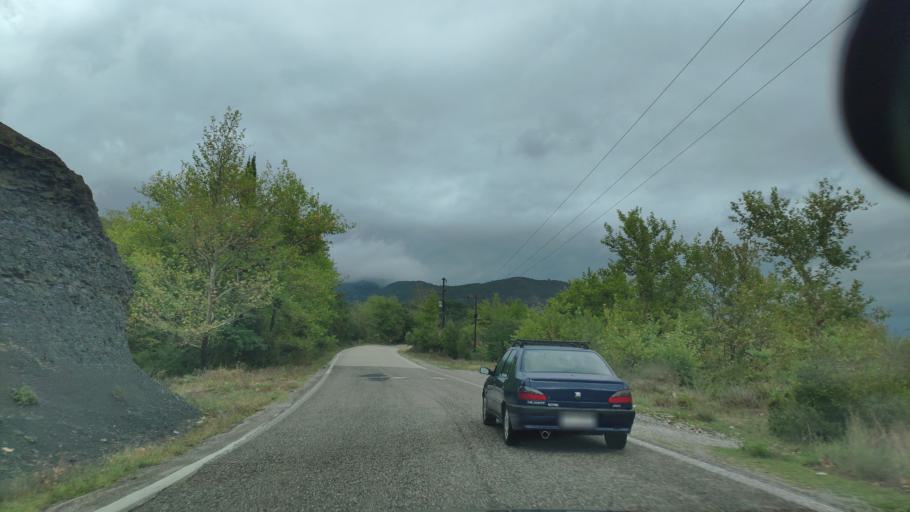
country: GR
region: West Greece
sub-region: Nomos Aitolias kai Akarnanias
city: Krikellos
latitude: 38.9610
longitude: 21.3331
